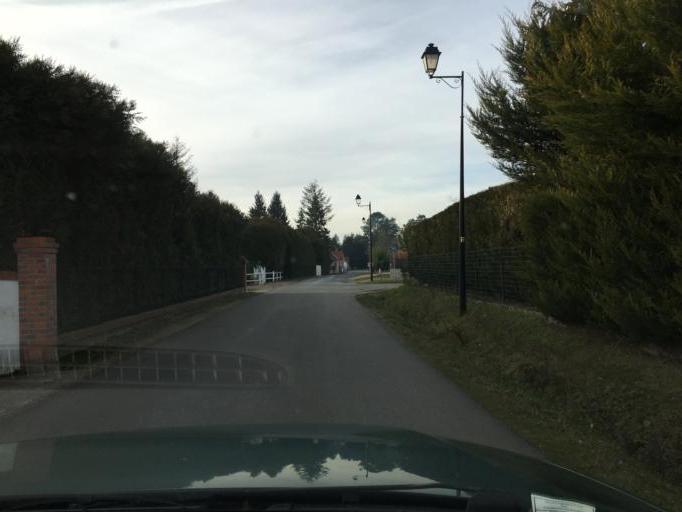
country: FR
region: Centre
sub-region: Departement du Loiret
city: Menestreau-en-Villette
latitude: 47.7005
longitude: 2.0167
